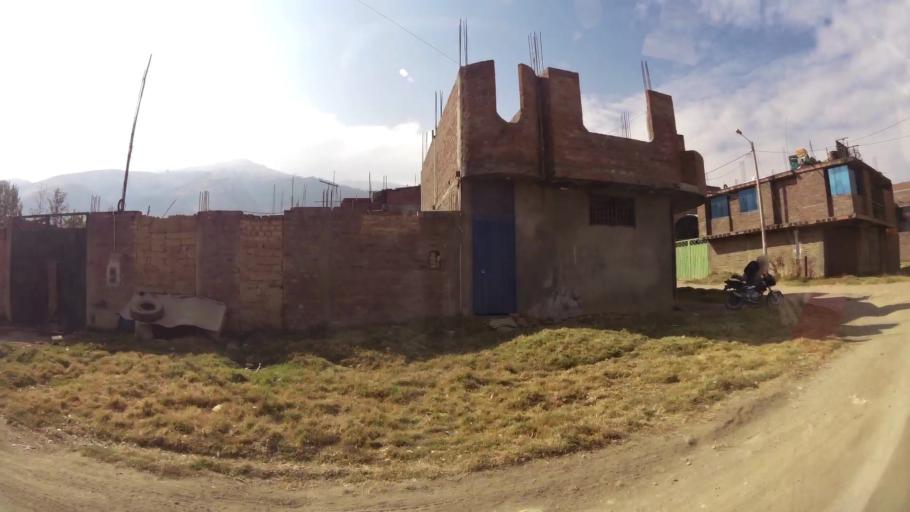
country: PE
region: Junin
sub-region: Provincia de Huancayo
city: Huancayo
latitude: -12.0553
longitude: -75.1930
